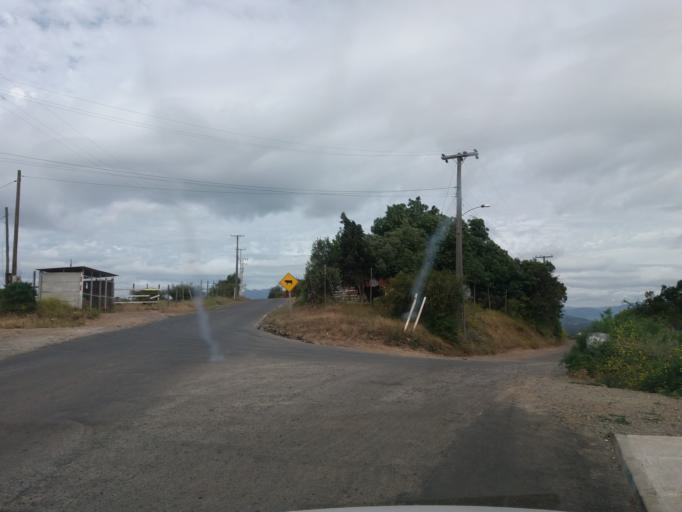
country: CL
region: Valparaiso
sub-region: Provincia de Quillota
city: Quillota
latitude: -32.9177
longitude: -71.3464
